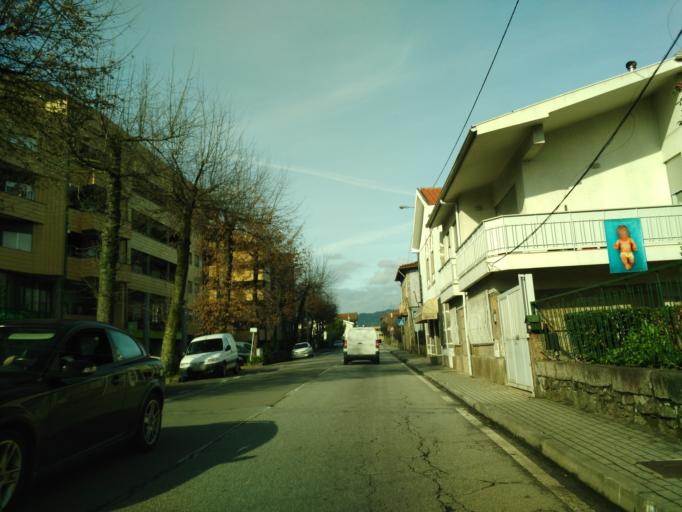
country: PT
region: Braga
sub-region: Guimaraes
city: Ponte
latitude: 41.4838
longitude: -8.3463
